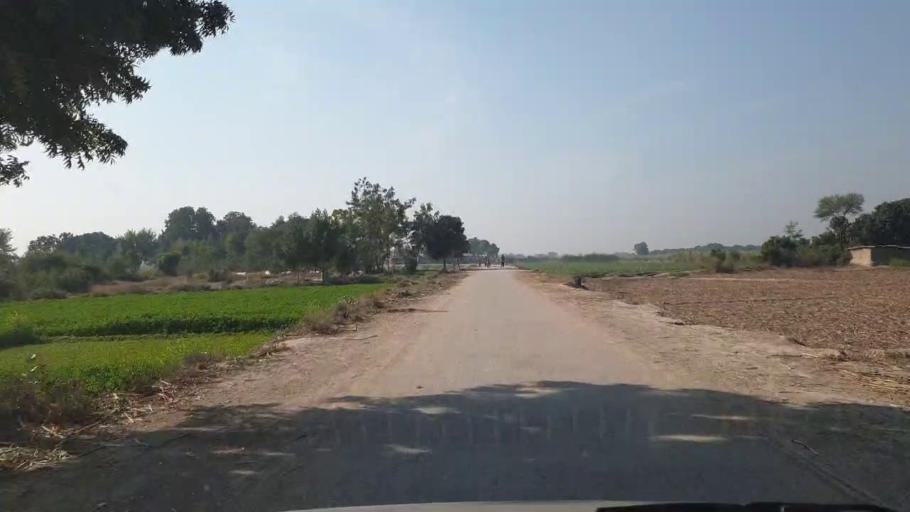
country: PK
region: Sindh
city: Tando Allahyar
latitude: 25.4133
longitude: 68.7432
